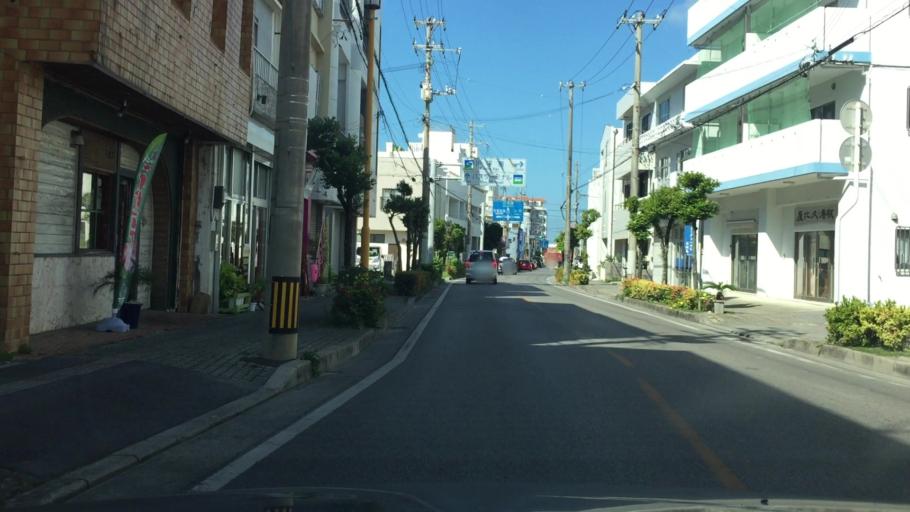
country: JP
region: Okinawa
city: Ishigaki
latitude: 24.3397
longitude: 124.1605
